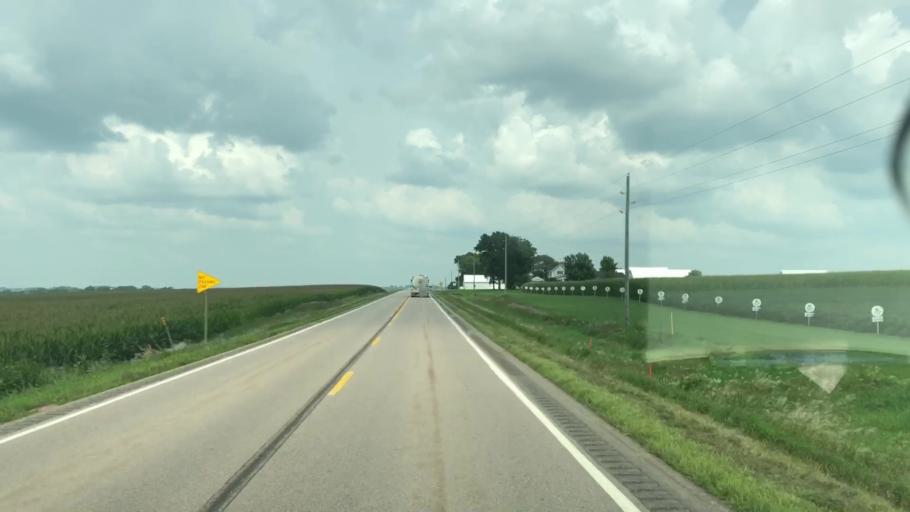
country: US
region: Iowa
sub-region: Plymouth County
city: Remsen
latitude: 42.8014
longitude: -95.9577
